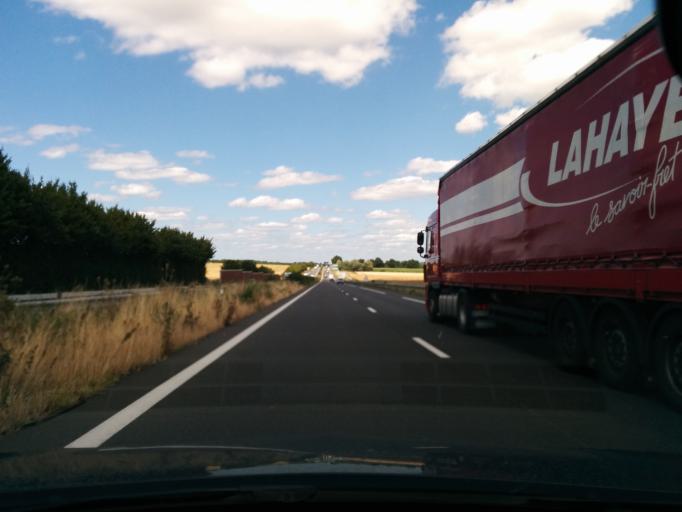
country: FR
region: Centre
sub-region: Departement du Cher
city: Massay
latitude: 47.1780
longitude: 2.0106
